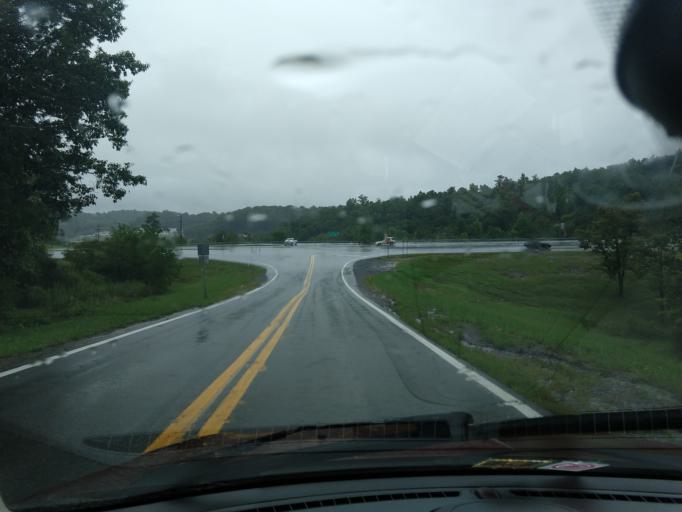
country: US
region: West Virginia
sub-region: Mercer County
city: Athens
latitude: 37.3635
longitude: -81.0373
